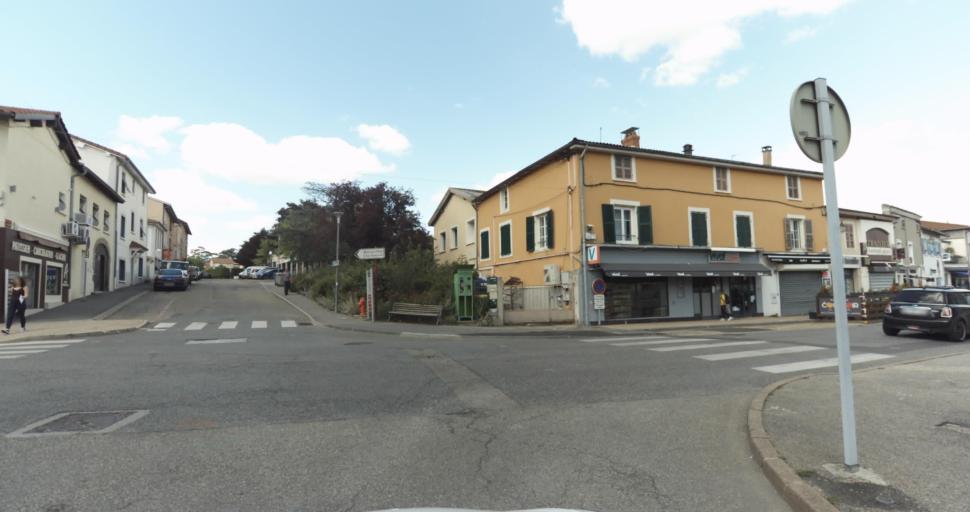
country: FR
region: Rhone-Alpes
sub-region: Departement du Rhone
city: Chaponost
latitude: 45.7120
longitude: 4.7456
